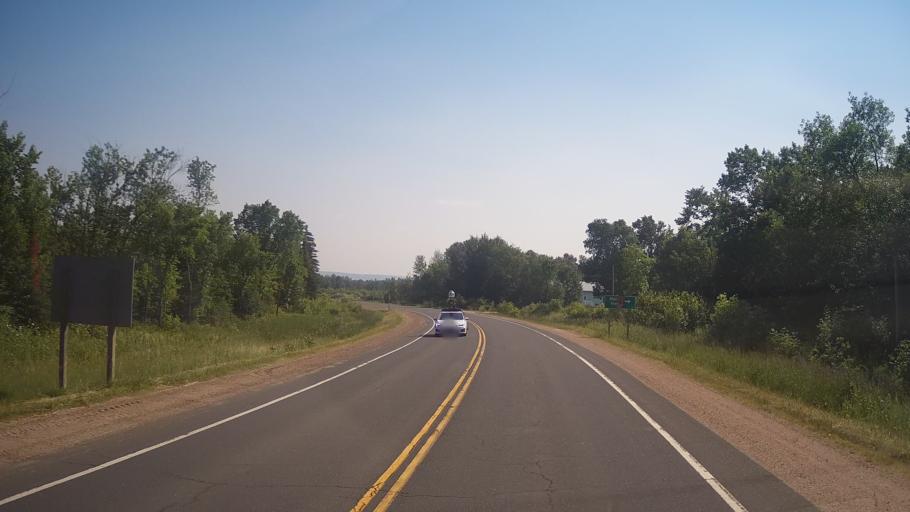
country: CA
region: Ontario
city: Petawawa
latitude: 45.5942
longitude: -77.4049
